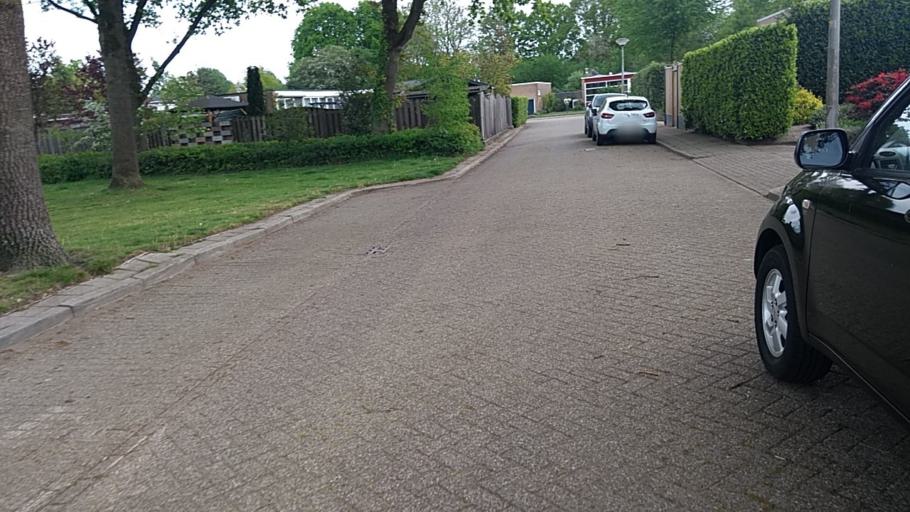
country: NL
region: Overijssel
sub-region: Gemeente Almelo
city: Almelo
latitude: 52.3729
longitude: 6.6712
